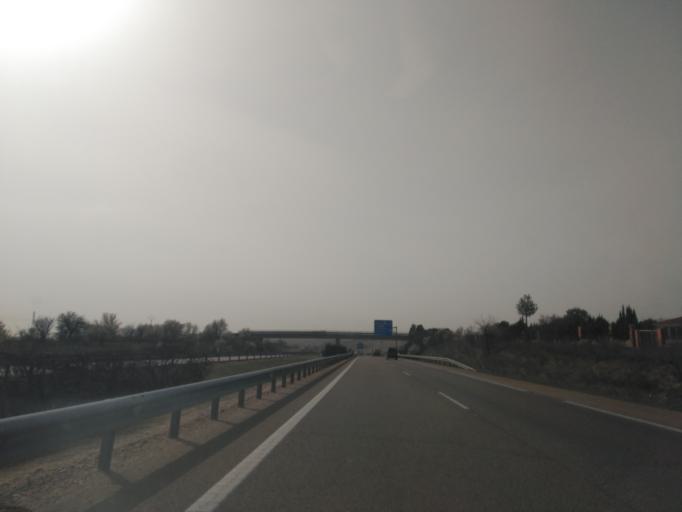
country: ES
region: Castille and Leon
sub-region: Provincia de Valladolid
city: Santovenia de Pisuerga
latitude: 41.6939
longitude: -4.7227
